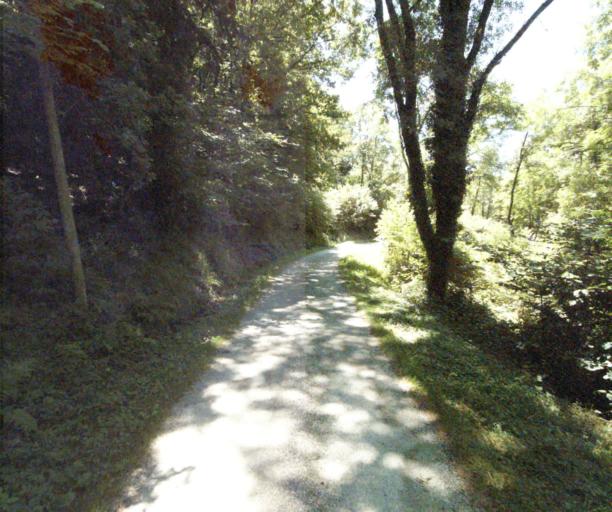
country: FR
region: Midi-Pyrenees
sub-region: Departement du Tarn
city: Dourgne
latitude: 43.4345
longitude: 2.1660
